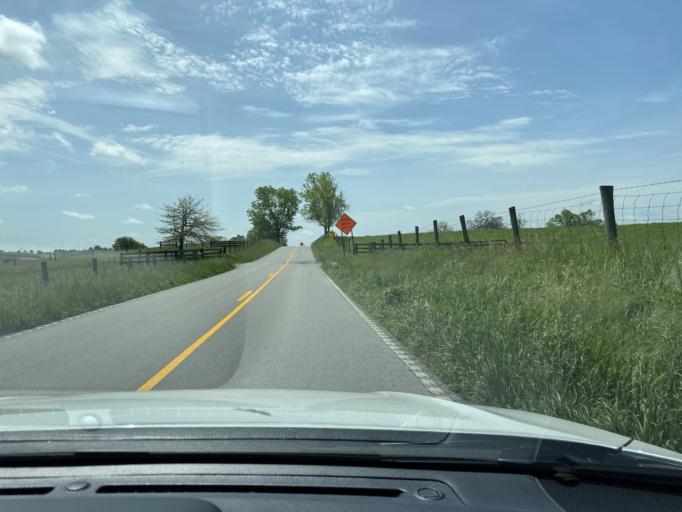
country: US
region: Kentucky
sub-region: Scott County
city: Georgetown
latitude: 38.2478
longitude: -84.5876
